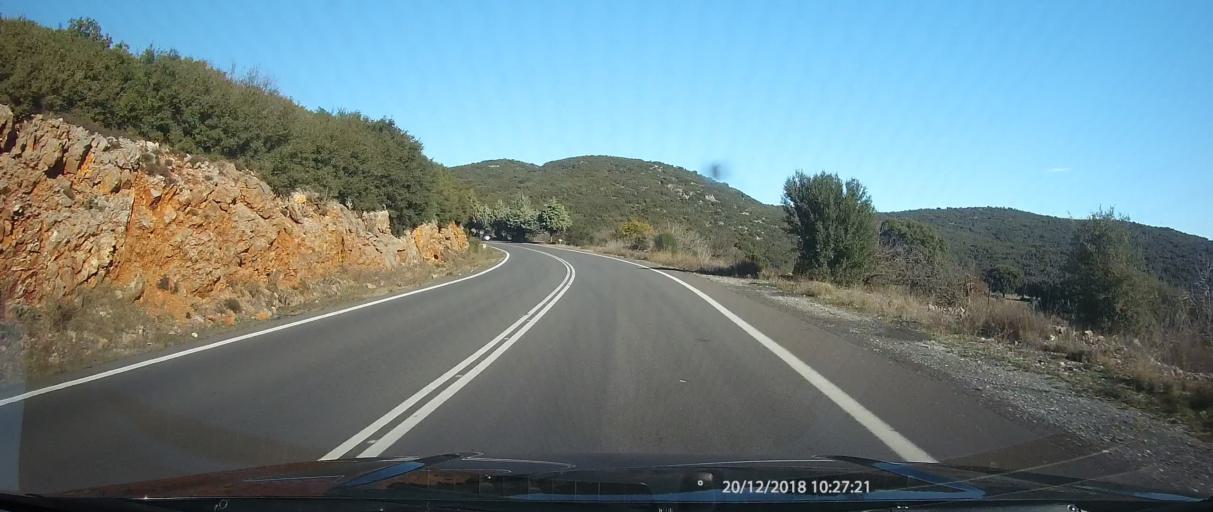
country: GR
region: Peloponnese
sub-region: Nomos Lakonias
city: Kariai
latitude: 37.2436
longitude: 22.4408
